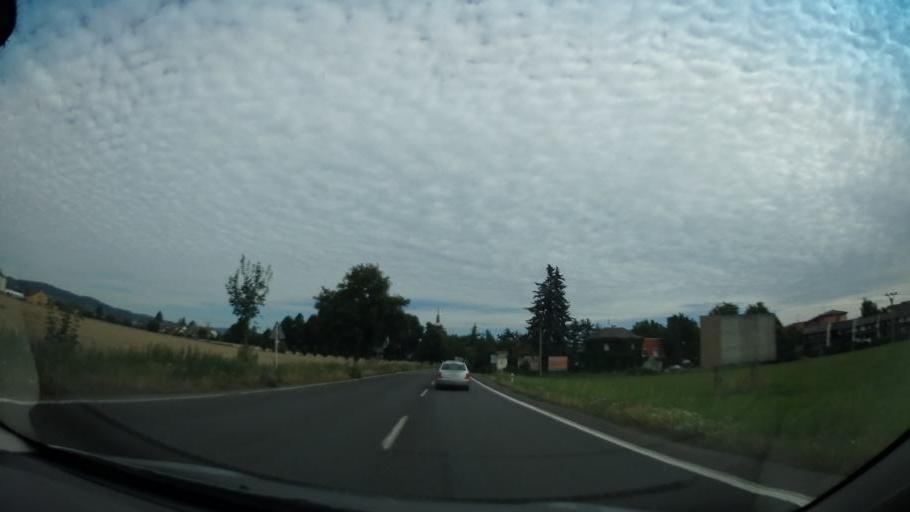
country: CZ
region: Olomoucky
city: Postrelmov
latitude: 49.9038
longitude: 16.9108
